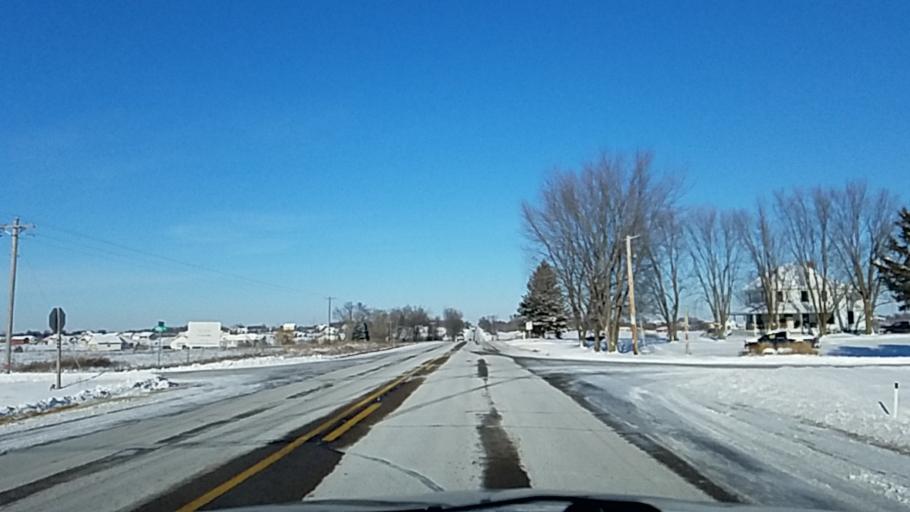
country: US
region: Wisconsin
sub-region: Saint Croix County
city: New Richmond
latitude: 45.0643
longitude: -92.5373
